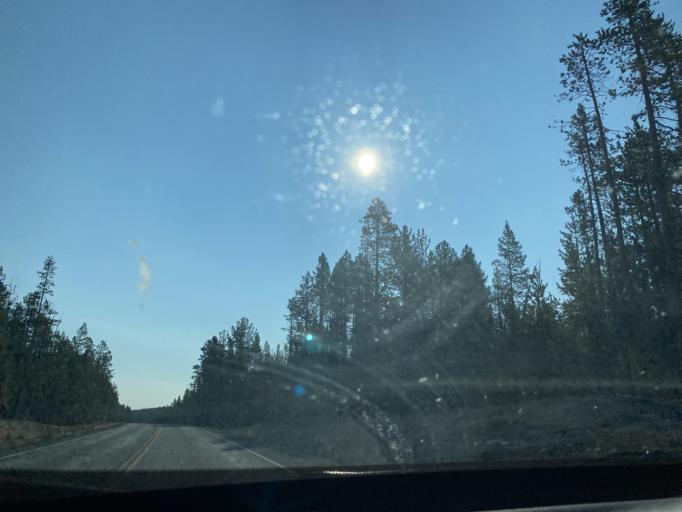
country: US
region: Oregon
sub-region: Deschutes County
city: Three Rivers
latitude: 43.7051
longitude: -121.2482
